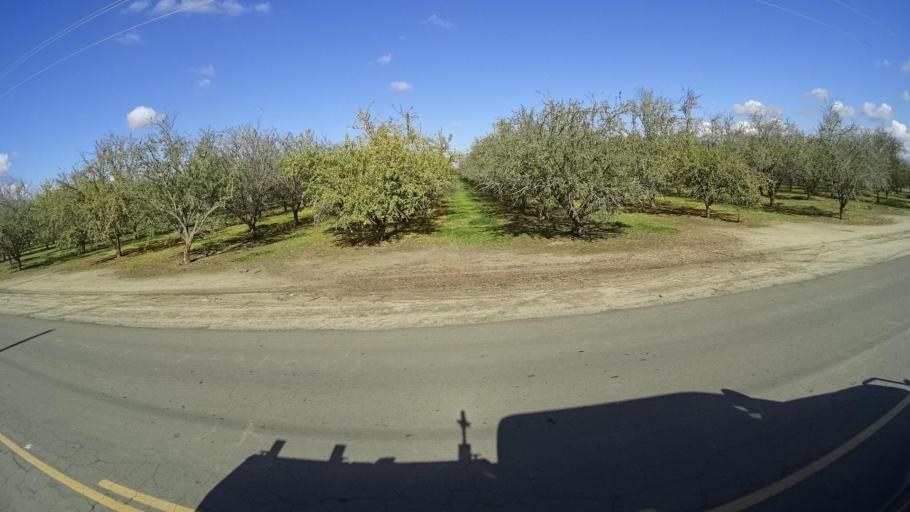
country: US
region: California
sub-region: Kern County
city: McFarland
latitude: 35.6888
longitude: -119.2596
